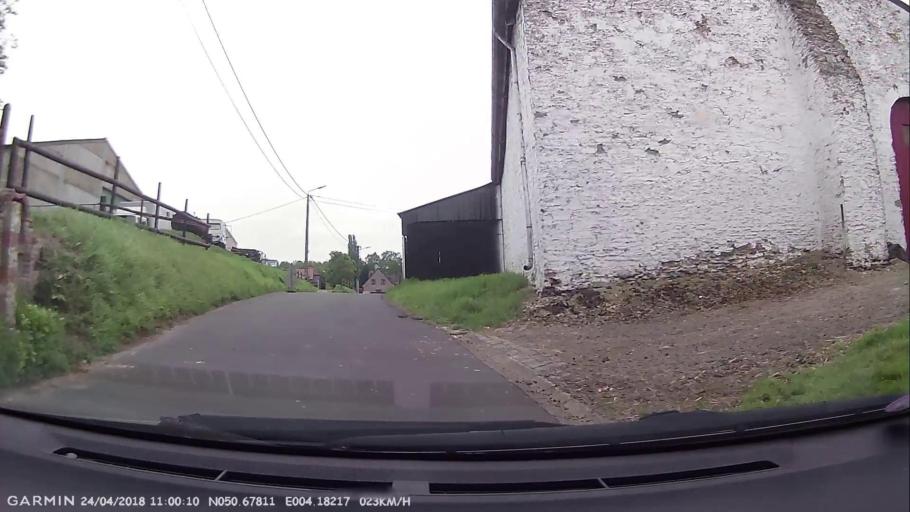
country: BE
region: Wallonia
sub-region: Province du Brabant Wallon
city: Tubize
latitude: 50.6781
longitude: 4.1824
